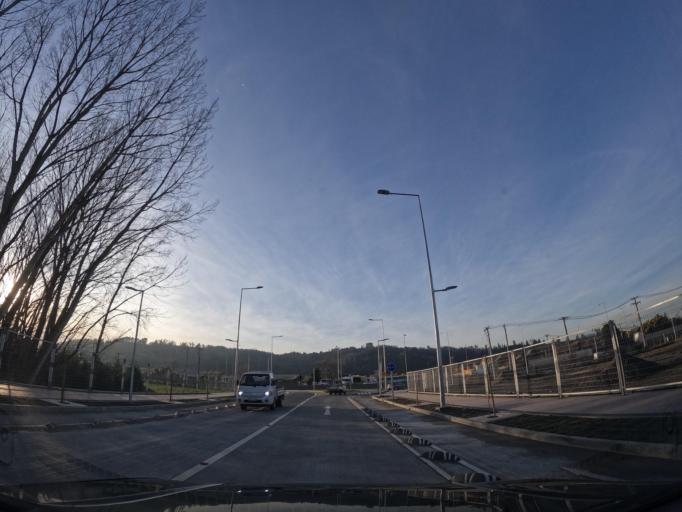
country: CL
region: Biobio
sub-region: Provincia de Concepcion
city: Concepcion
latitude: -36.8192
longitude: -73.0081
